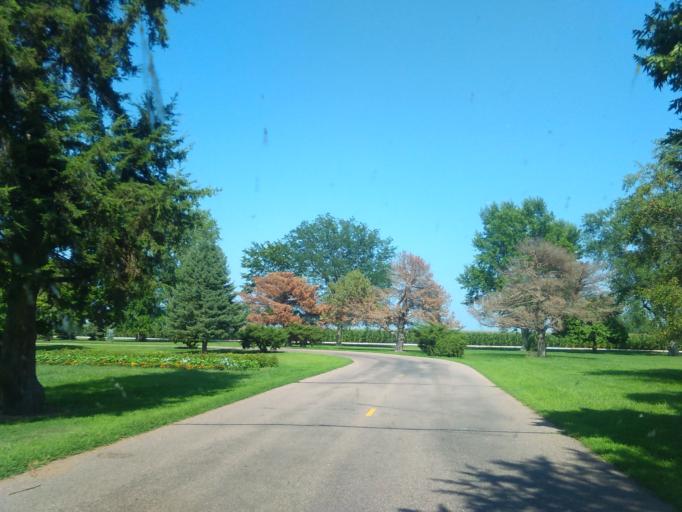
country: US
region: Nebraska
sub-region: Buffalo County
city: Kearney
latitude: 40.6427
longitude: -99.0050
